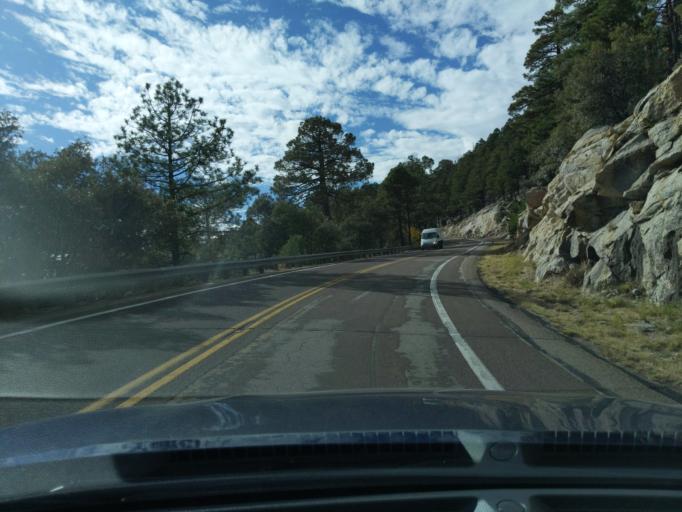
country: US
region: Arizona
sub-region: Pima County
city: Tanque Verde
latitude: 32.4107
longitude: -110.7167
